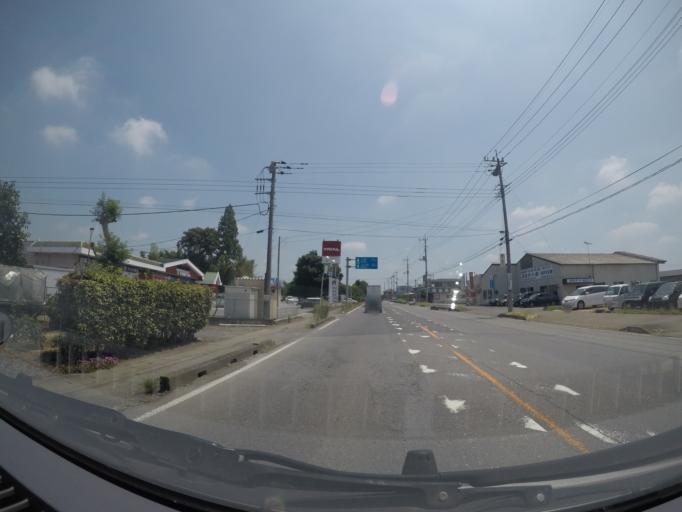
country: JP
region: Ibaraki
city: Ishige
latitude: 36.1888
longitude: 139.8891
